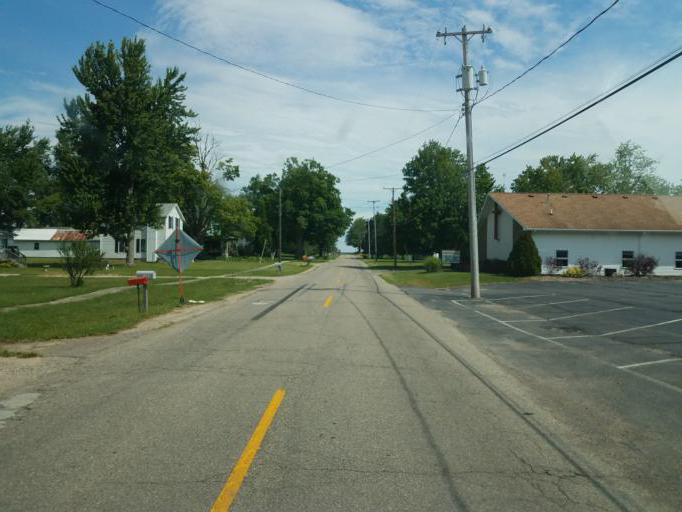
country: US
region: Michigan
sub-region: Barry County
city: Nashville
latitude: 42.6310
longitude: -85.0247
